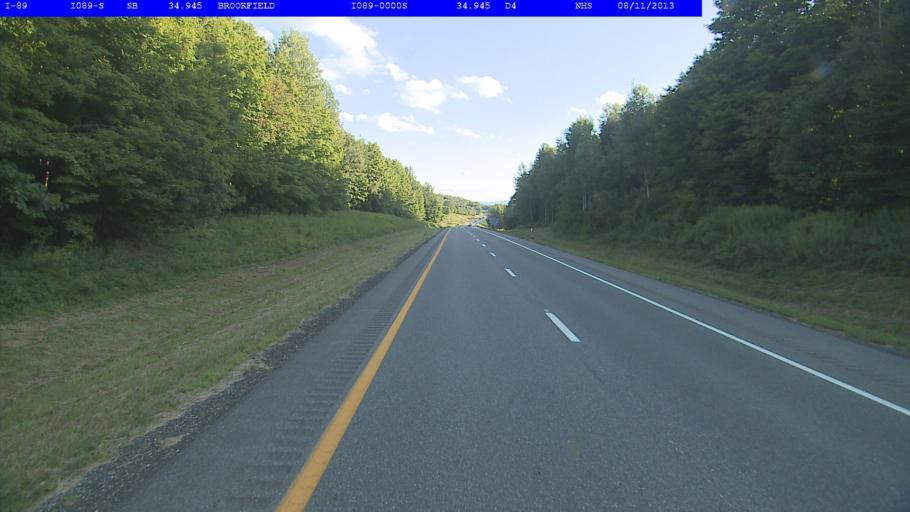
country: US
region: Vermont
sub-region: Orange County
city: Randolph
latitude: 44.0030
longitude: -72.6226
